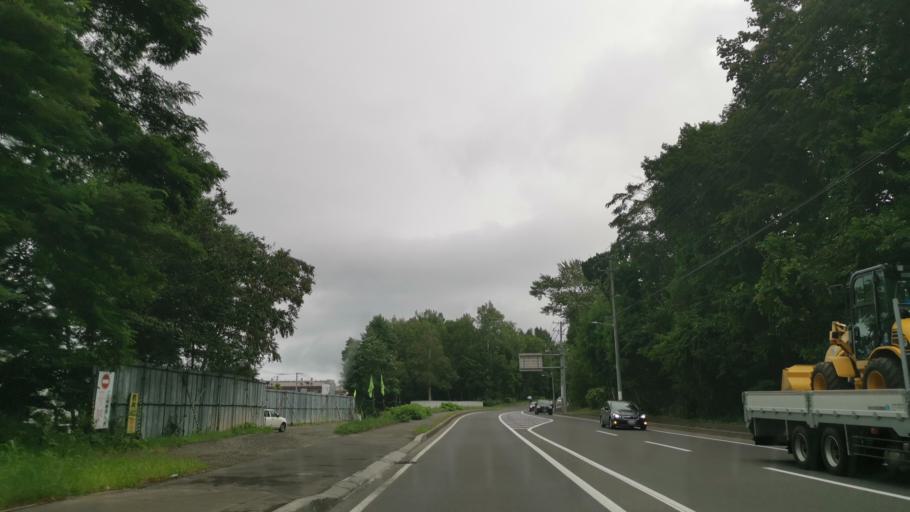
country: JP
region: Hokkaido
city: Sapporo
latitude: 42.9808
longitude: 141.3534
